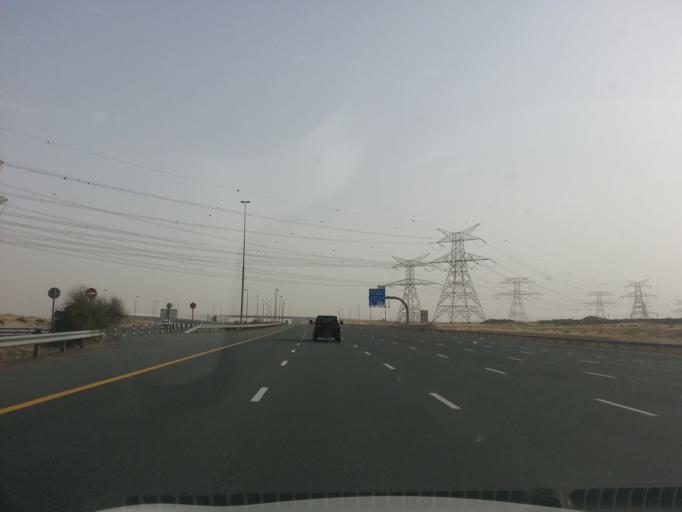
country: AE
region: Dubai
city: Dubai
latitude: 24.9851
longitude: 55.2439
